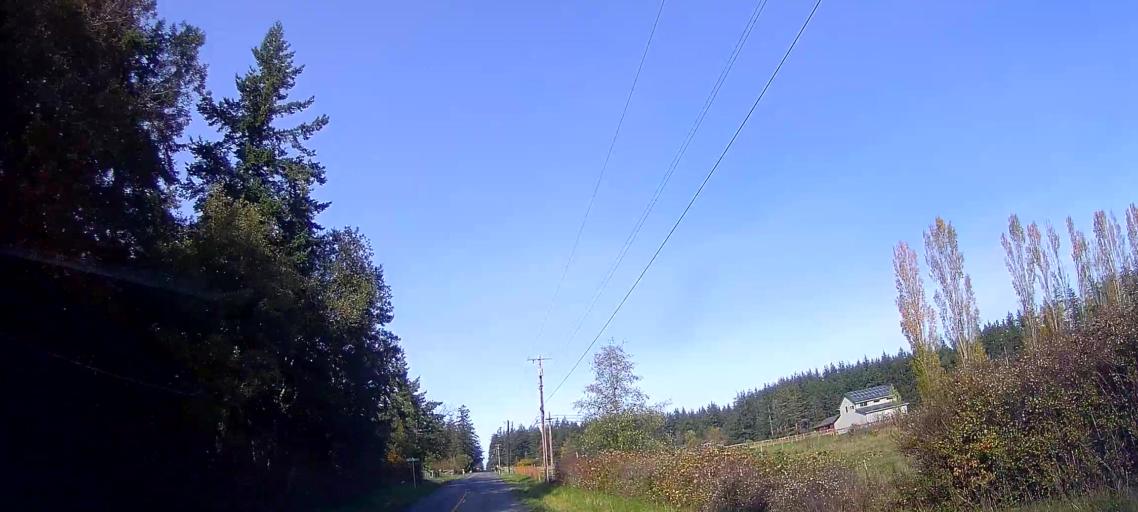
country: US
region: Washington
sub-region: Island County
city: Camano
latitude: 48.2028
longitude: -122.4563
